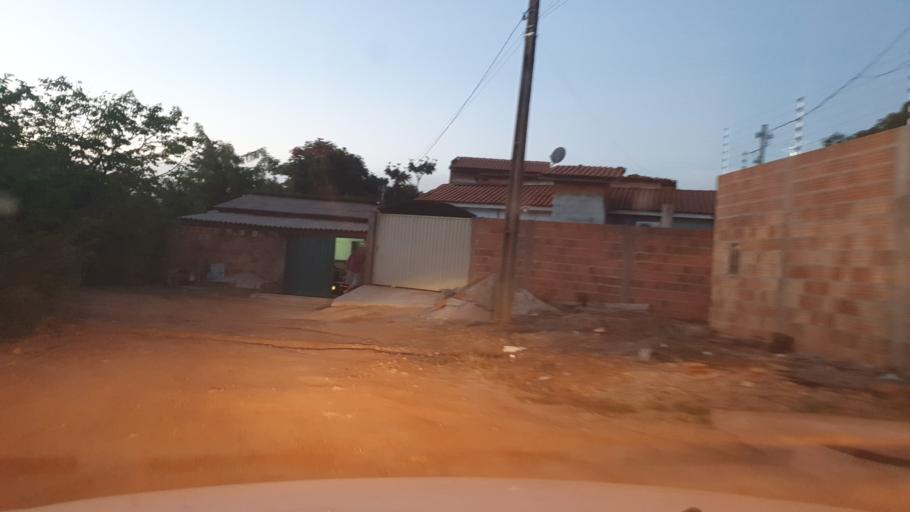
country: BR
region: Mato Grosso
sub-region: Pontes E Lacerda
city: Pontes e Lacerda
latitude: -15.2475
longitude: -59.3252
